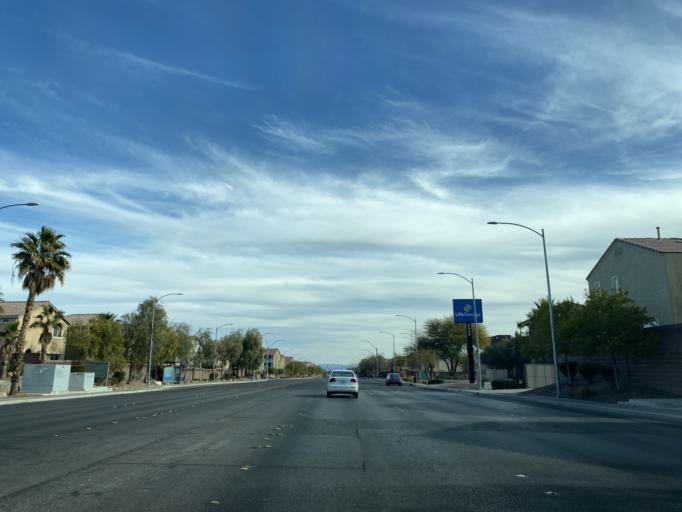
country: US
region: Nevada
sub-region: Clark County
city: Enterprise
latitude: 36.0560
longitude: -115.2357
